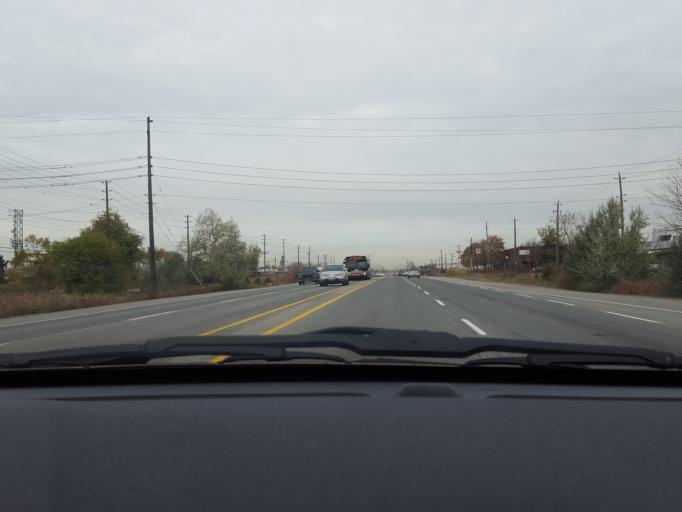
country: CA
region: Ontario
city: Etobicoke
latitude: 43.6934
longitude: -79.5844
